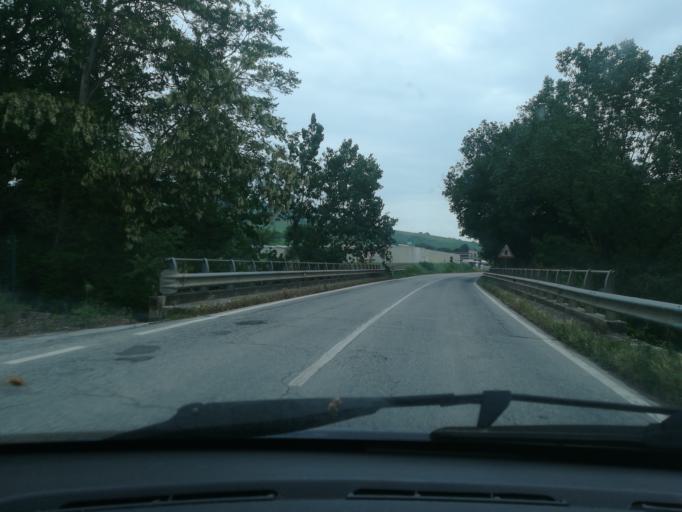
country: IT
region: The Marches
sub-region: Provincia di Macerata
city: San Severino Marche
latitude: 43.2575
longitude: 13.2346
